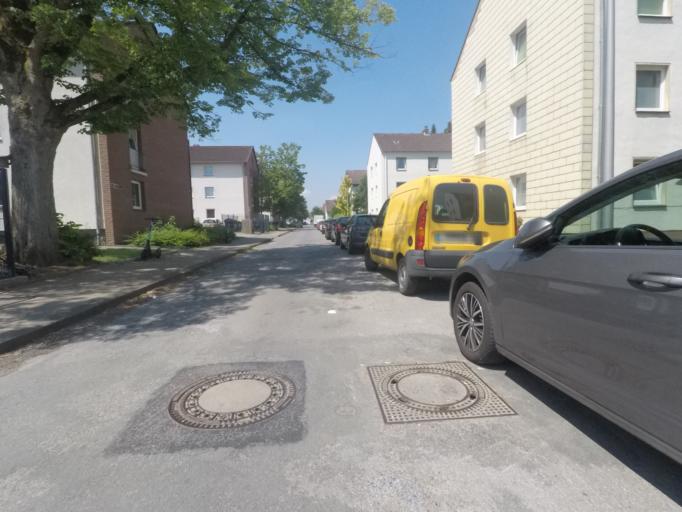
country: DE
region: North Rhine-Westphalia
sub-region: Regierungsbezirk Detmold
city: Bielefeld
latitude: 52.0154
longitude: 8.5704
